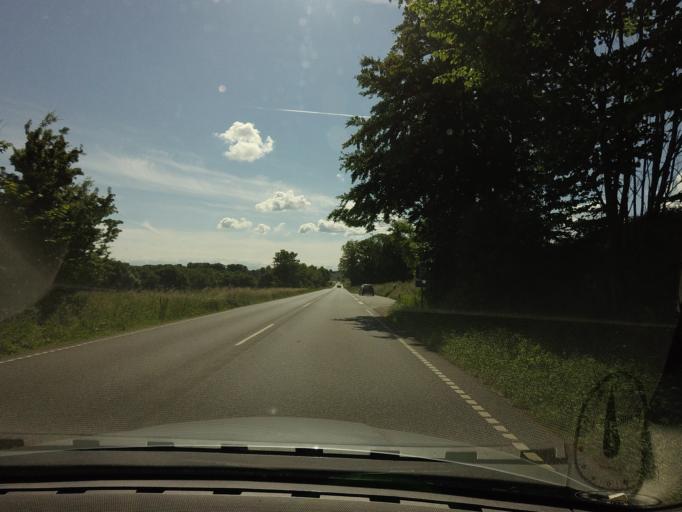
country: DK
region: Central Jutland
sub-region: Syddjurs Kommune
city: Ebeltoft
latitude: 56.3307
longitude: 10.7251
